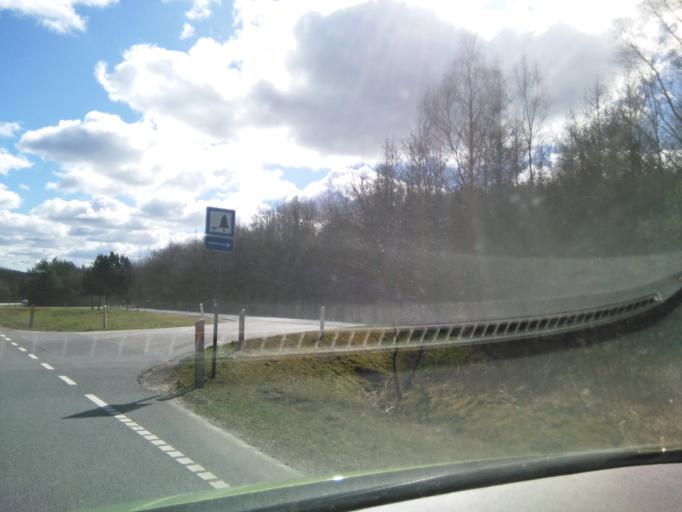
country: DK
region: Central Jutland
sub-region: Silkeborg Kommune
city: Virklund
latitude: 56.0731
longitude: 9.5749
